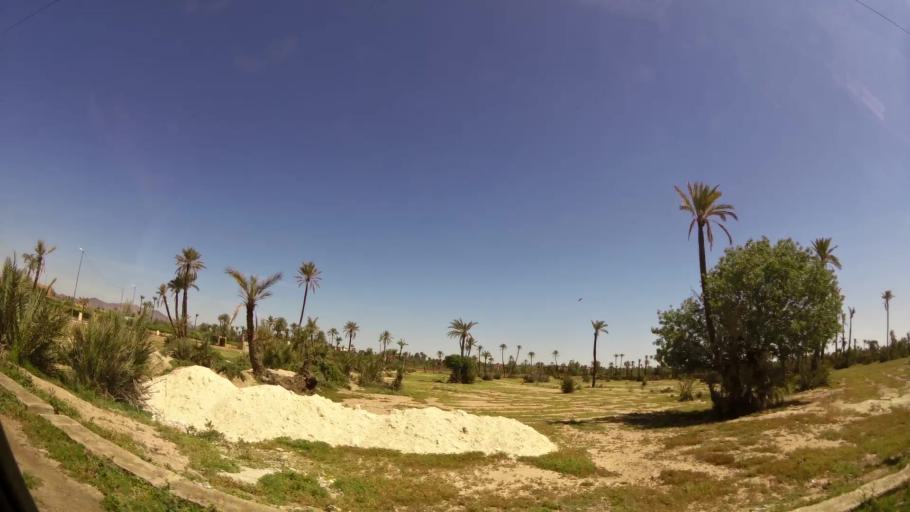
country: MA
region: Marrakech-Tensift-Al Haouz
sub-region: Marrakech
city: Marrakesh
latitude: 31.6770
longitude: -7.9857
